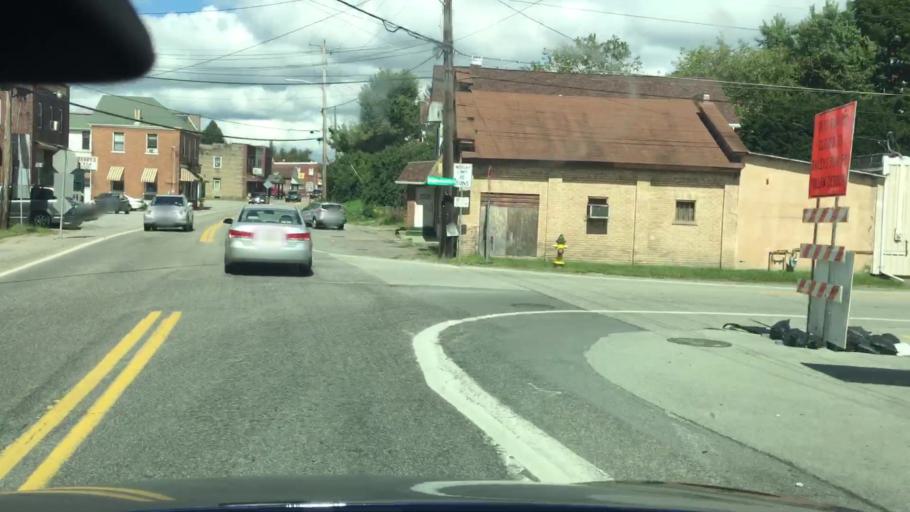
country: US
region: Pennsylvania
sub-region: Allegheny County
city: Russellton
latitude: 40.6172
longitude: -79.8337
